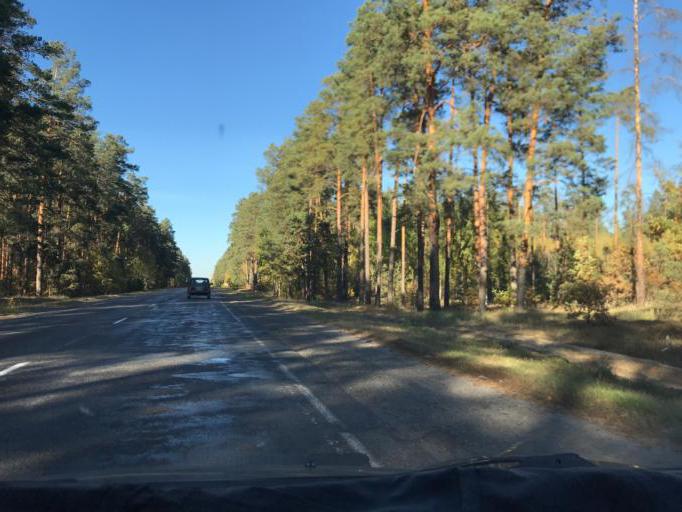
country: BY
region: Gomel
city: Kalinkavichy
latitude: 52.0570
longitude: 29.3611
